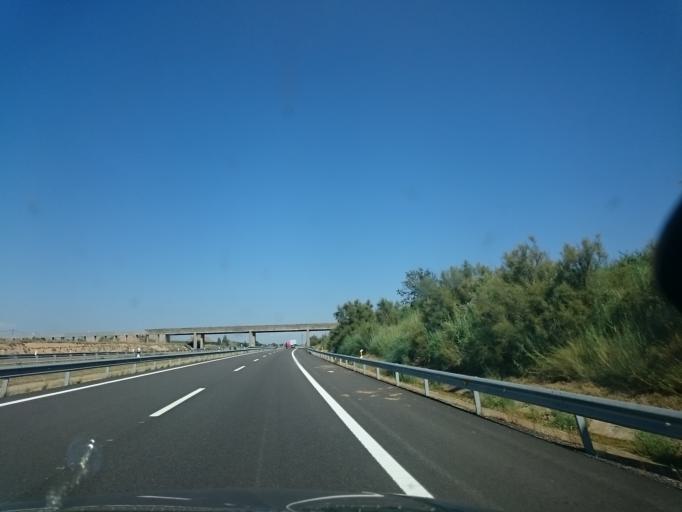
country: ES
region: Catalonia
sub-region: Provincia de Lleida
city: Seros
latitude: 41.4957
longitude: 0.3848
